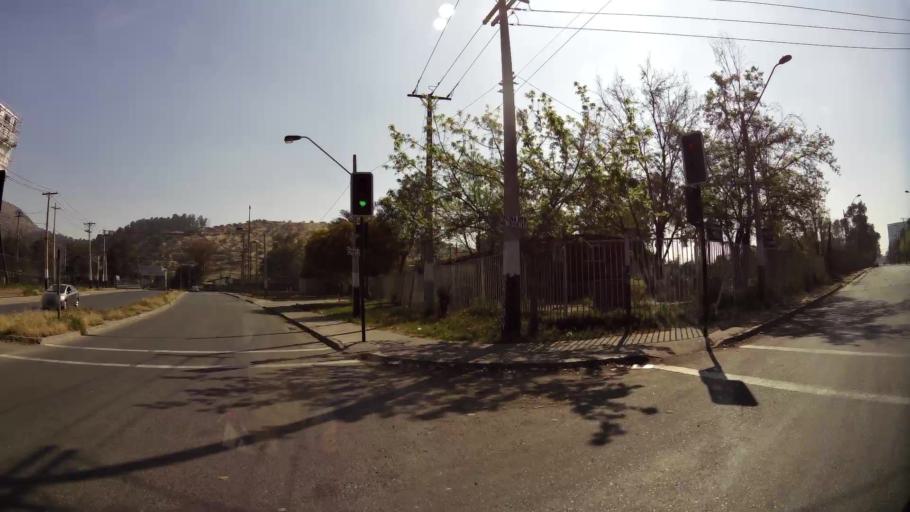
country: CL
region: Santiago Metropolitan
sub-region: Provincia de Santiago
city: Lo Prado
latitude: -33.3742
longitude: -70.6955
